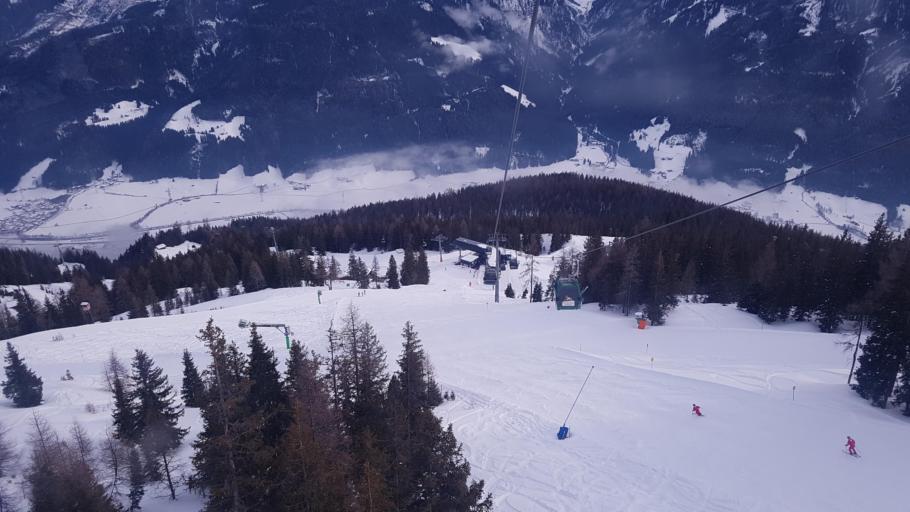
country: AT
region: Salzburg
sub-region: Politischer Bezirk Zell am See
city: Neukirchen am Grossvenediger
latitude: 47.2751
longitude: 12.3009
